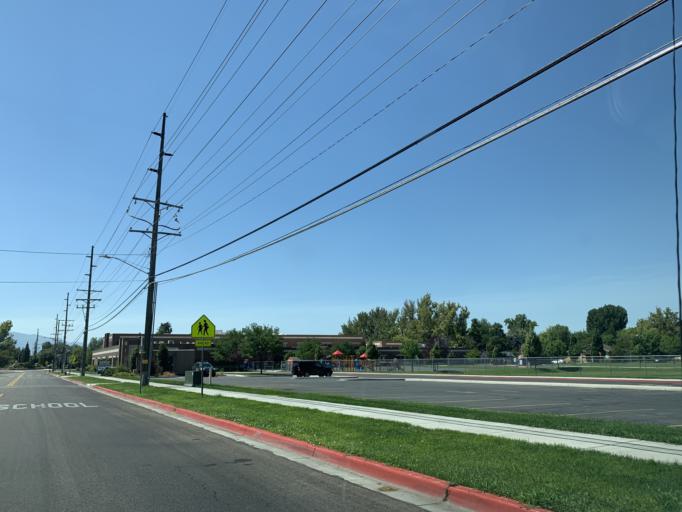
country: US
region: Utah
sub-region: Utah County
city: Provo
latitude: 40.2358
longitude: -111.6466
